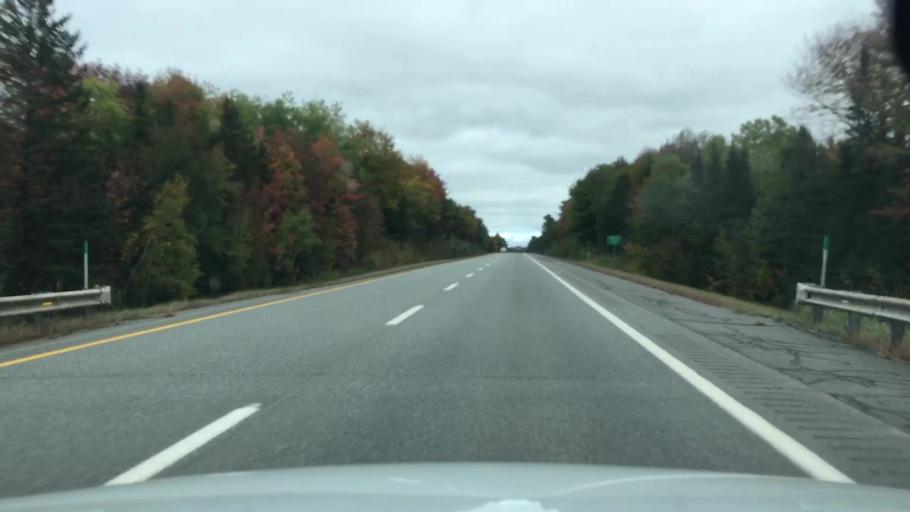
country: US
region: Maine
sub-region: Penobscot County
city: Plymouth
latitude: 44.7891
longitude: -69.1801
